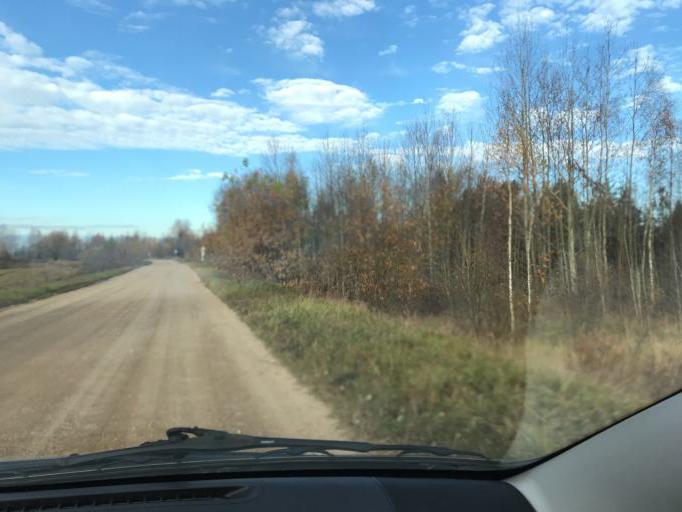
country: BY
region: Vitebsk
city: Haradok
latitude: 55.4542
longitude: 30.0222
